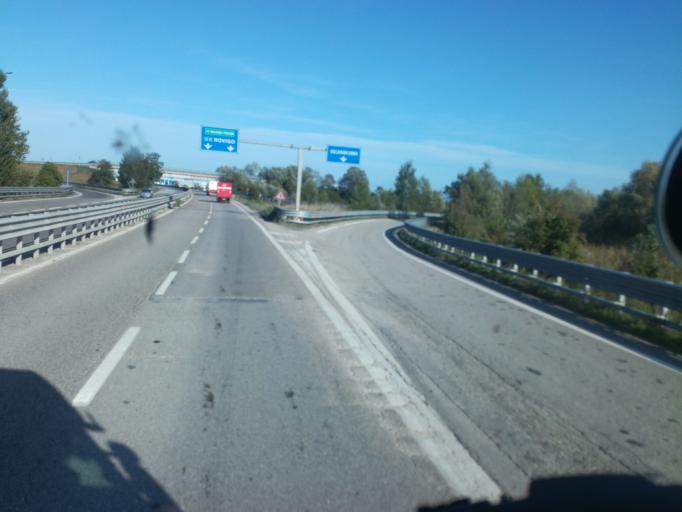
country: IT
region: Veneto
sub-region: Provincia di Rovigo
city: Villamarzana
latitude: 45.0198
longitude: 11.6987
